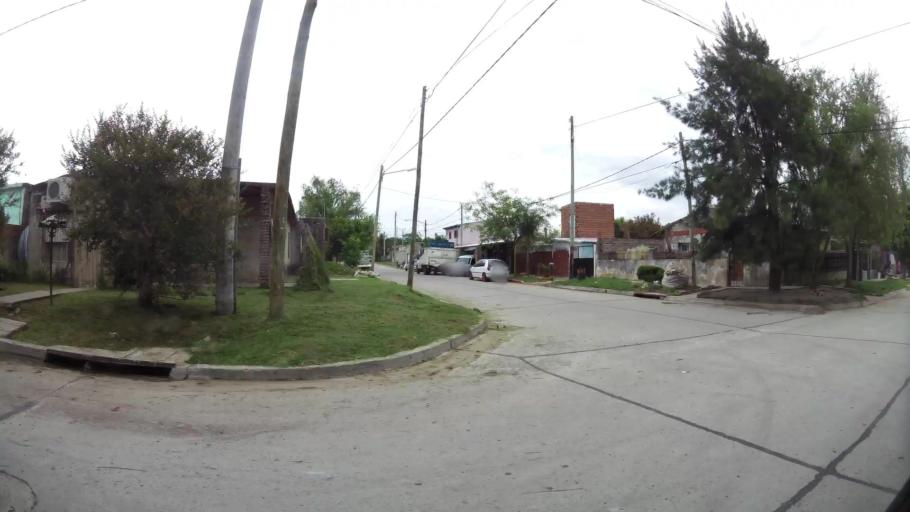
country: AR
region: Buenos Aires
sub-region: Partido de Campana
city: Campana
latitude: -34.1813
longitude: -58.9463
